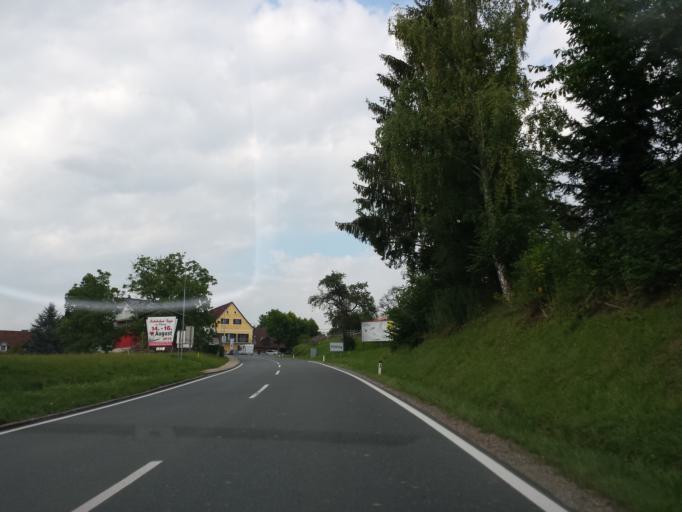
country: AT
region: Styria
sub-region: Politischer Bezirk Deutschlandsberg
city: Stainz
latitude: 46.9020
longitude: 15.2728
